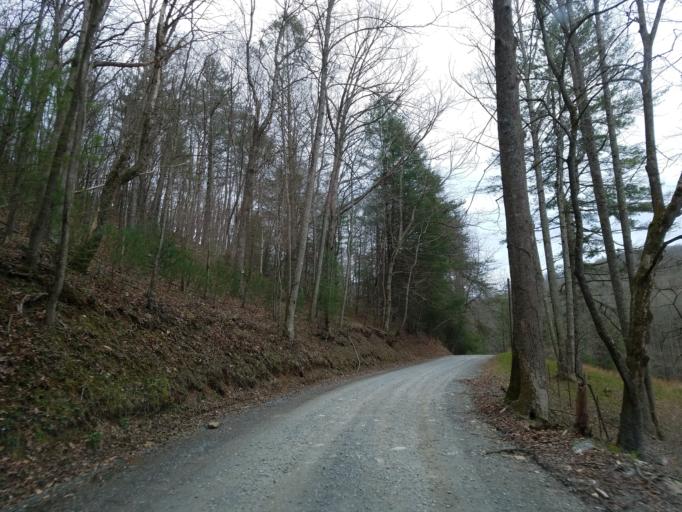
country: US
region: Georgia
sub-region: Fannin County
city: Blue Ridge
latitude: 34.7366
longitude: -84.2821
